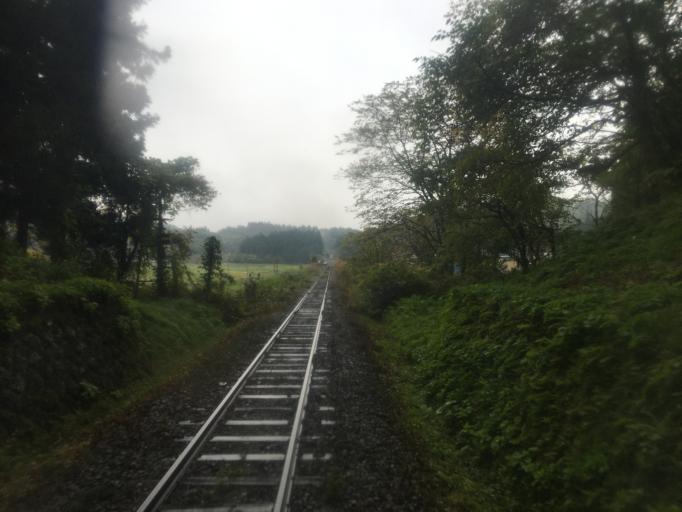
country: JP
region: Yamagata
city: Shinjo
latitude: 38.7473
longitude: 140.2064
